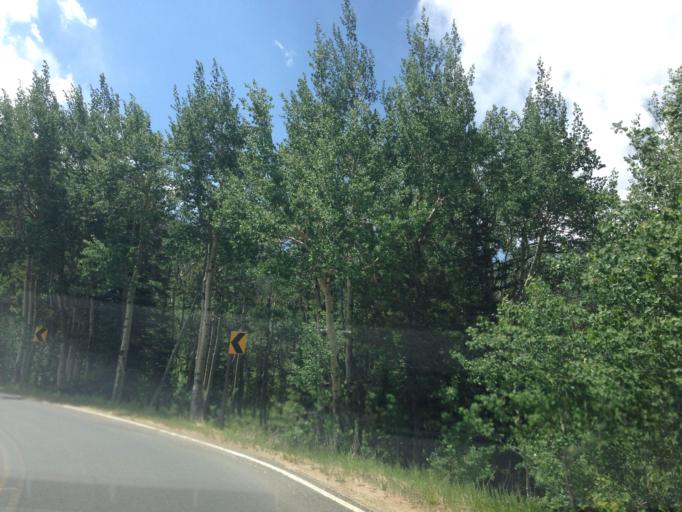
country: US
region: Colorado
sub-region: Larimer County
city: Estes Park
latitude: 40.3971
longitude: -105.6506
